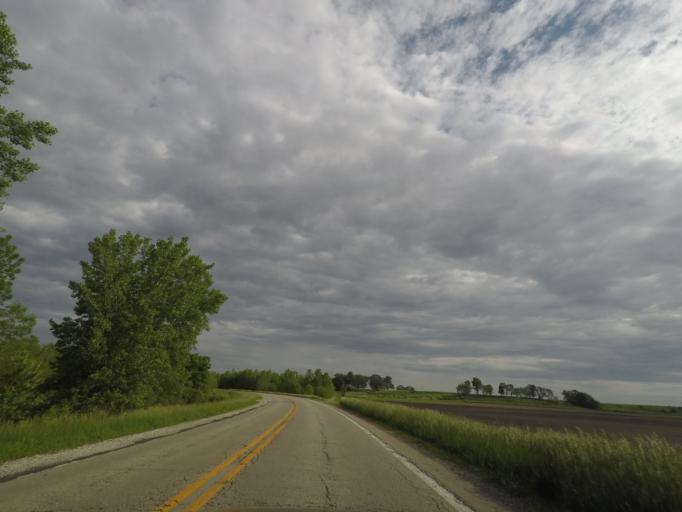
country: US
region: Illinois
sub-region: Logan County
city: Mount Pulaski
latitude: 40.0583
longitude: -89.2820
